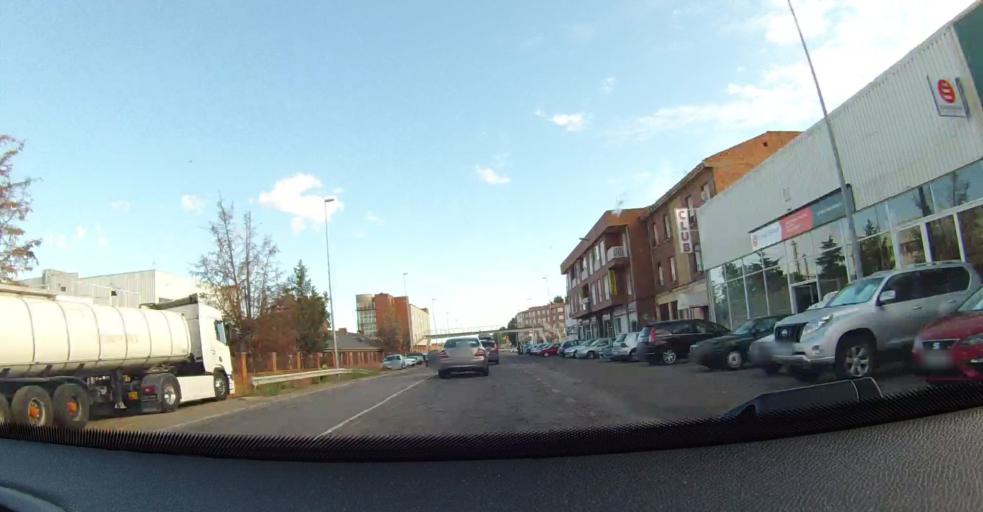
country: ES
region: Castille and Leon
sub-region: Provincia de Leon
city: Leon
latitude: 42.5798
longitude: -5.5837
